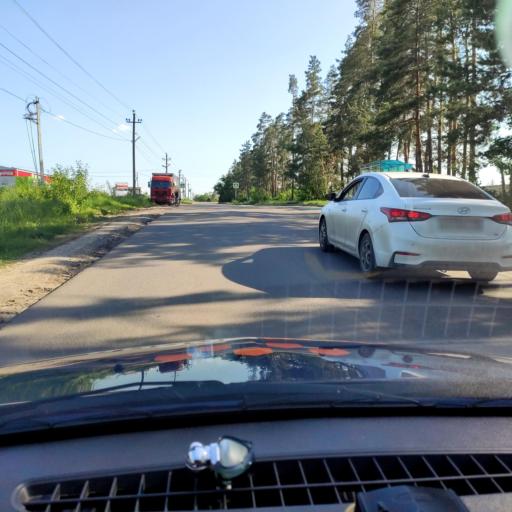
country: RU
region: Voronezj
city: Podgornoye
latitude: 51.8139
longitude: 39.1405
